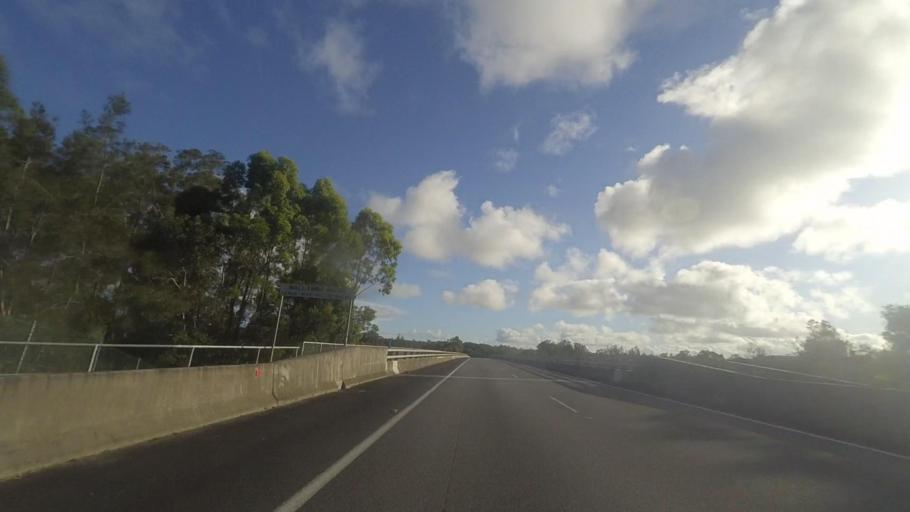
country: AU
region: New South Wales
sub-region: Great Lakes
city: Nabiac
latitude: -32.1044
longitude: 152.3745
